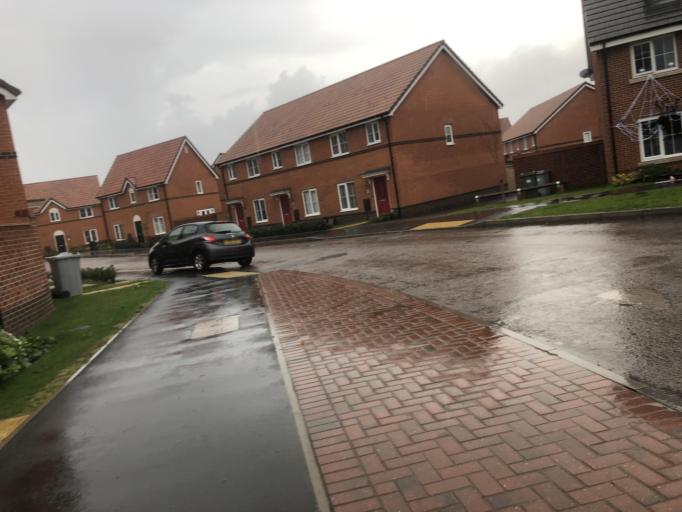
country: GB
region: England
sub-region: Norfolk
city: Spixworth
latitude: 52.6577
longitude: 1.3453
